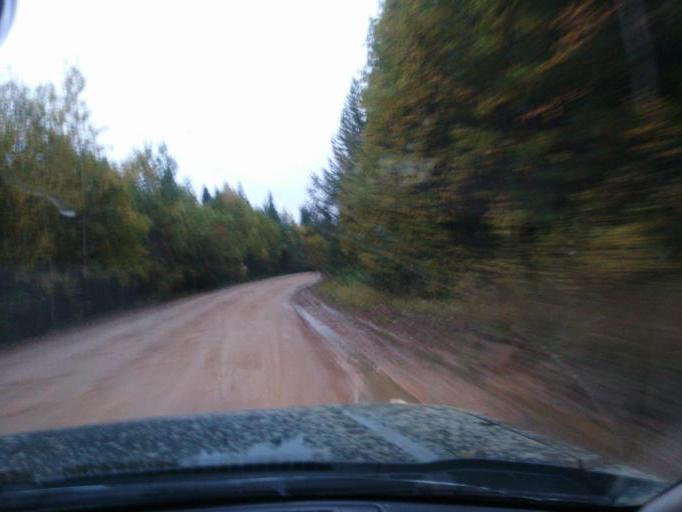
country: RU
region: Sverdlovsk
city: Sylva
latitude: 57.8124
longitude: 58.6015
